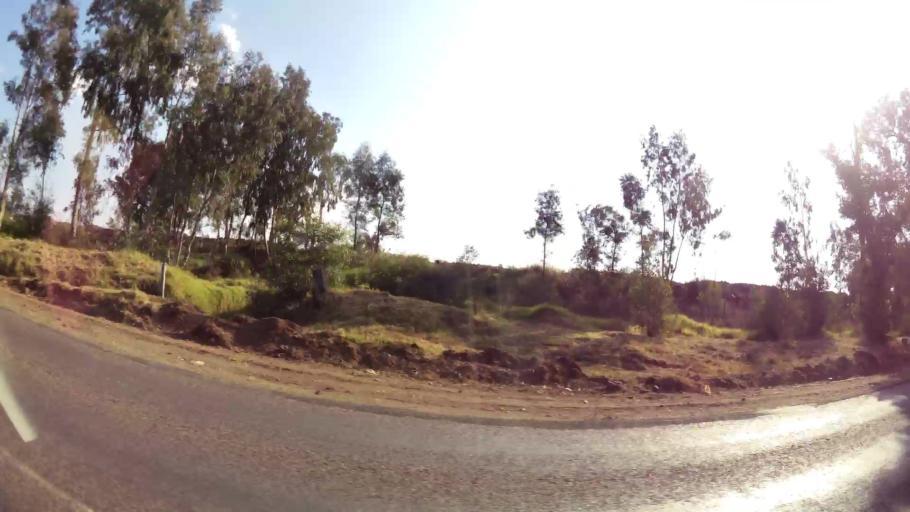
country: ZA
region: Gauteng
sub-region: Ekurhuleni Metropolitan Municipality
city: Tembisa
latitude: -25.9365
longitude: 28.2327
